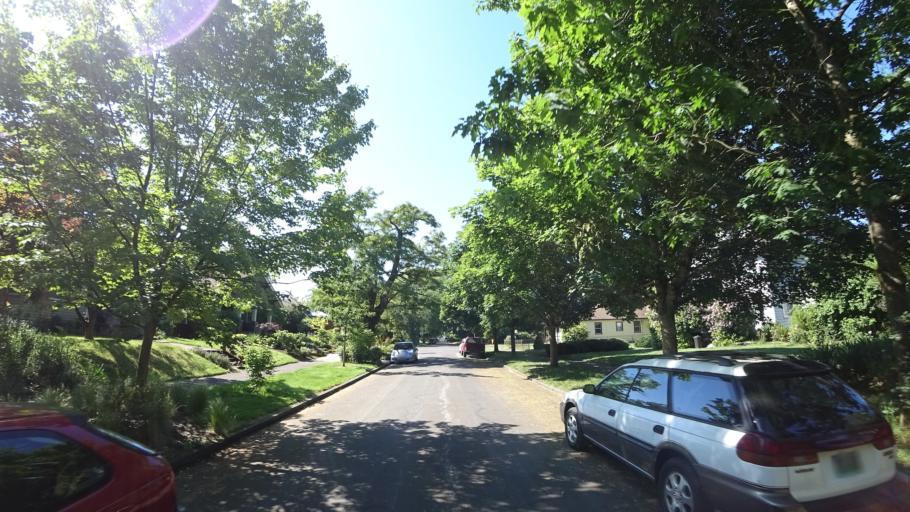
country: US
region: Oregon
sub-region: Multnomah County
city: Portland
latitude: 45.5671
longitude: -122.6637
